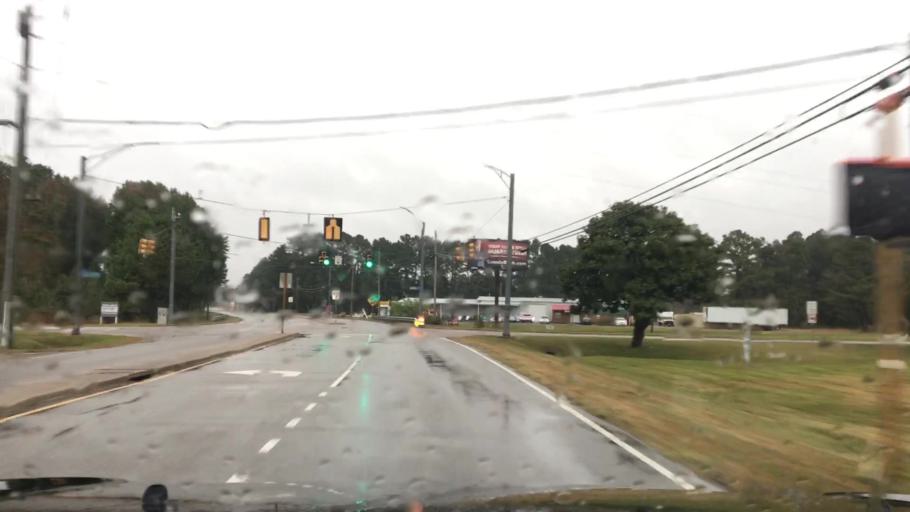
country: US
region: Virginia
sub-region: City of Chesapeake
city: Chesapeake
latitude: 36.6755
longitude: -76.2267
